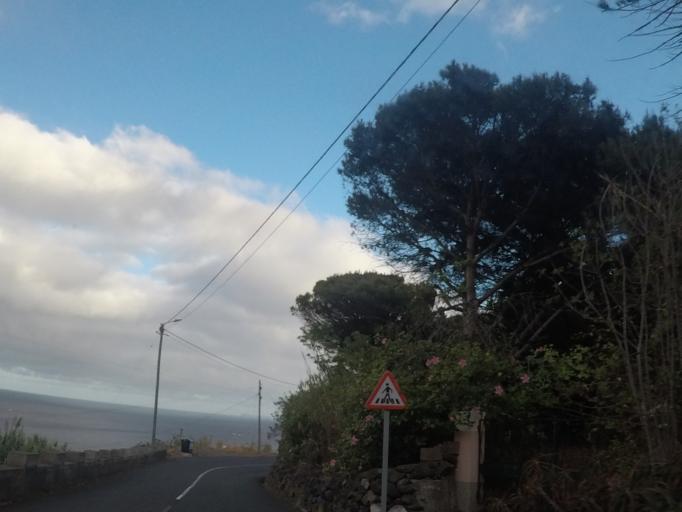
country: PT
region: Madeira
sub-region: Santa Cruz
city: Santa Cruz
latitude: 32.6707
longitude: -16.8048
